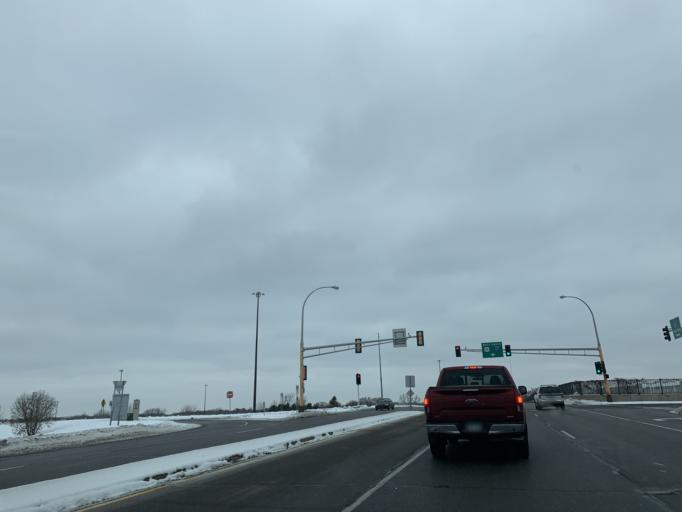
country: US
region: Minnesota
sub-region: Anoka County
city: Coon Rapids
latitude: 45.1508
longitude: -93.2752
